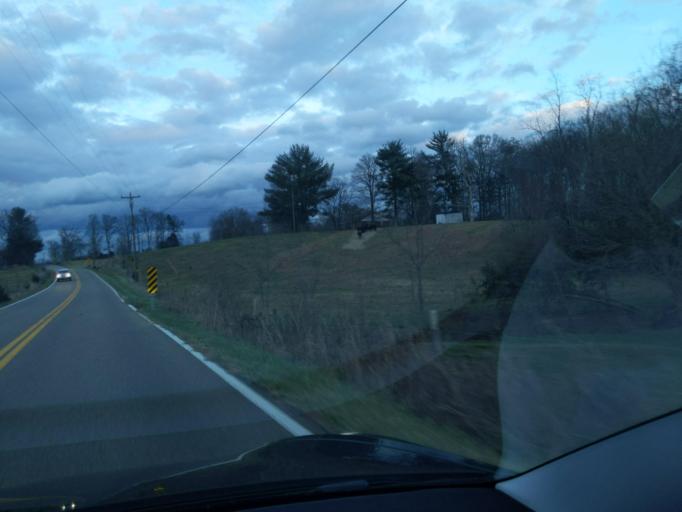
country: US
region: Tennessee
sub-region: Jefferson County
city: White Pine
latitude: 36.0872
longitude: -83.3656
